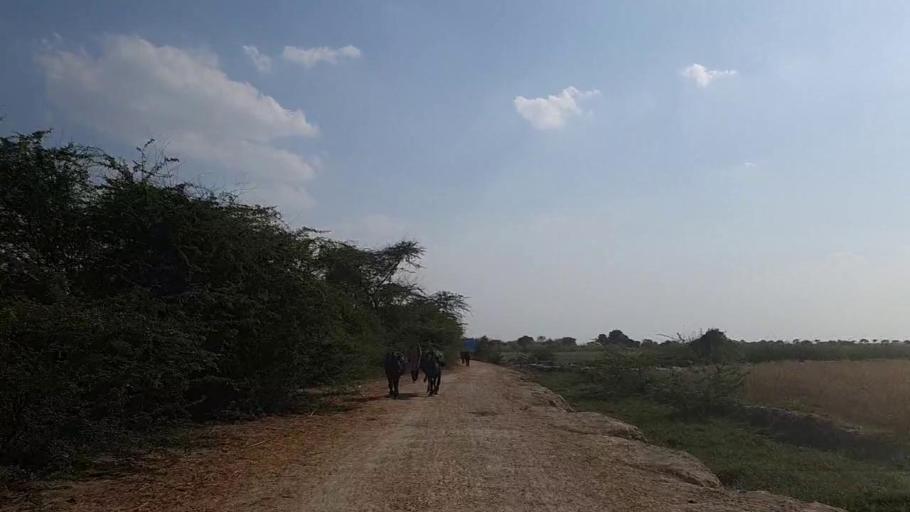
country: PK
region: Sindh
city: Jati
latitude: 24.4781
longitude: 68.3387
